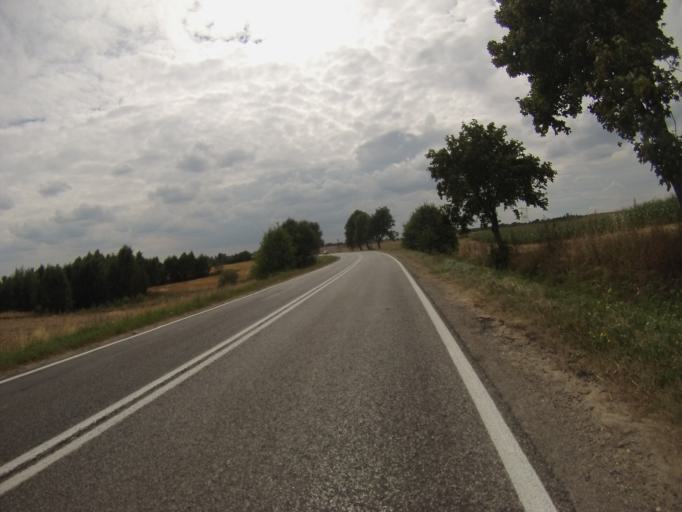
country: PL
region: Swietokrzyskie
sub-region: Powiat kielecki
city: Lagow
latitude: 50.7489
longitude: 21.0721
